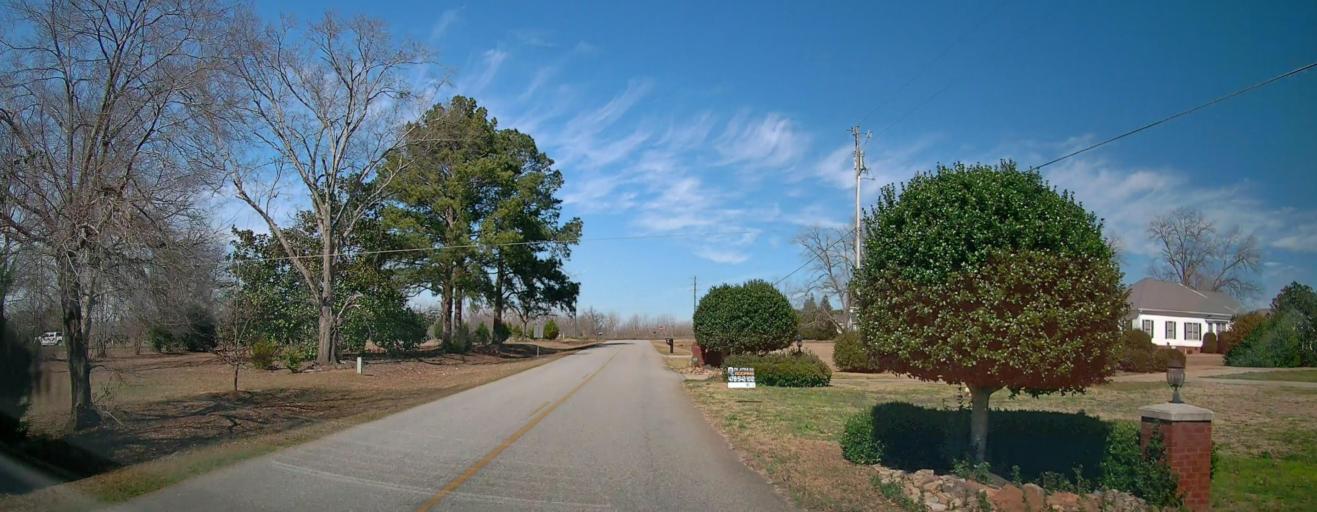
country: US
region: Georgia
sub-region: Houston County
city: Perry
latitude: 32.4530
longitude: -83.6970
